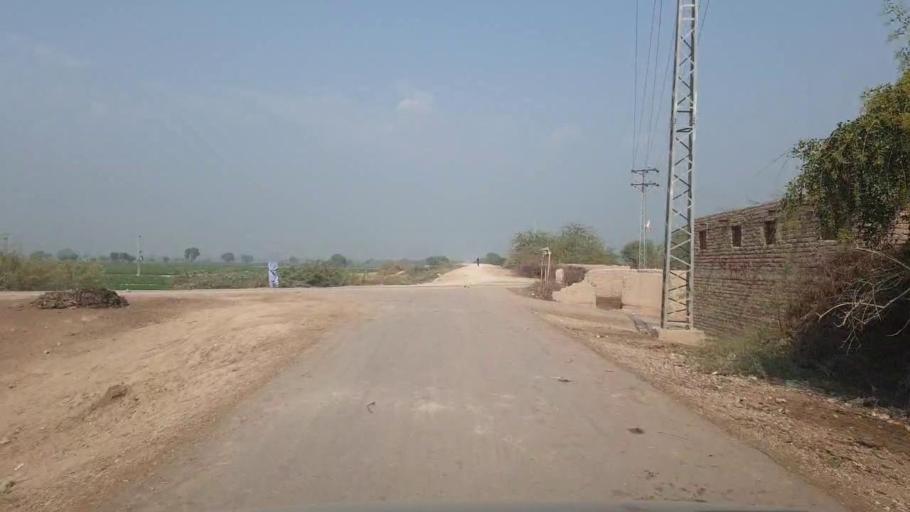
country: PK
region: Sindh
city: Hala
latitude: 25.8011
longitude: 68.4015
